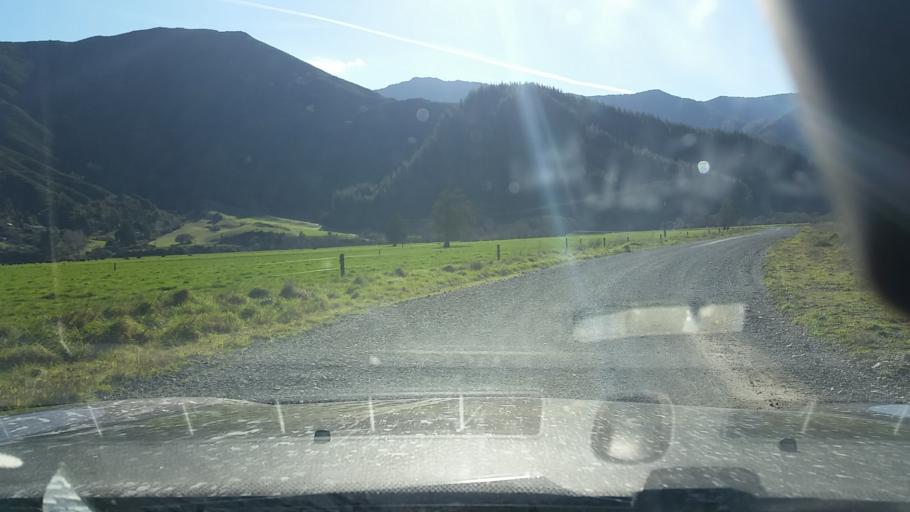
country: NZ
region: Marlborough
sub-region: Marlborough District
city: Picton
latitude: -41.2735
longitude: 173.7296
